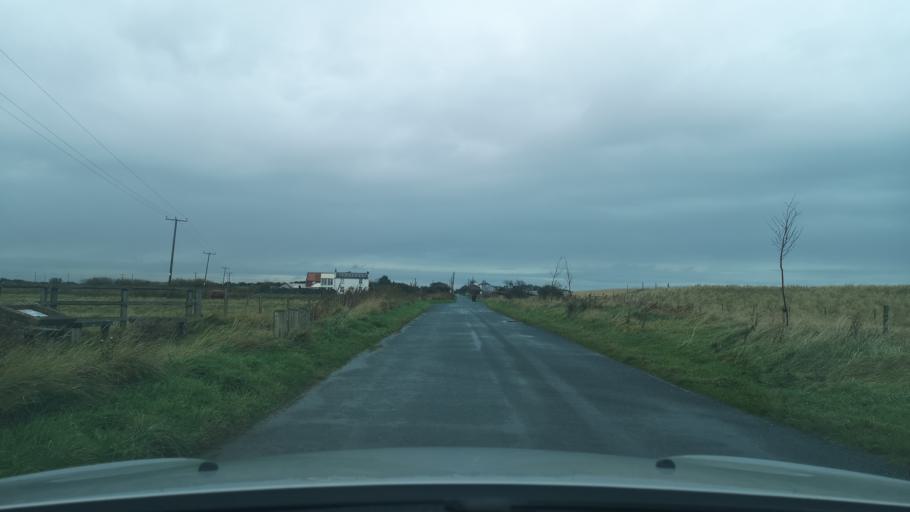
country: GB
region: England
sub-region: East Riding of Yorkshire
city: Easington
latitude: 53.6172
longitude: 0.1401
